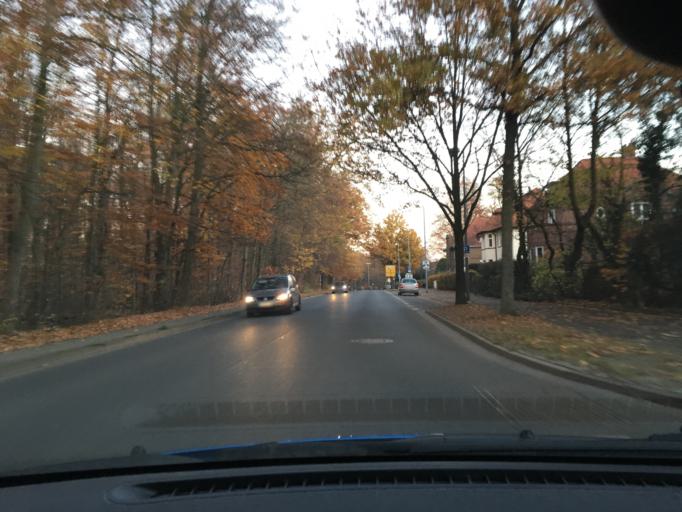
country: DE
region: Lower Saxony
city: Uelzen
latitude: 52.9750
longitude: 10.5494
